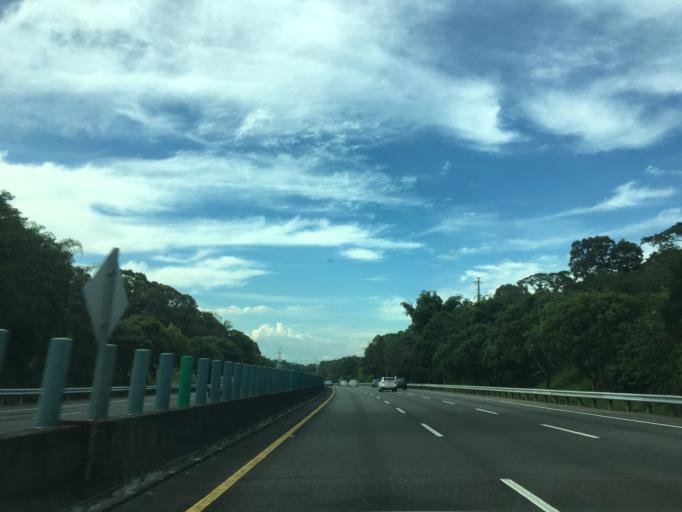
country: TW
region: Taiwan
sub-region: Chiayi
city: Jiayi Shi
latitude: 23.5494
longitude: 120.5046
